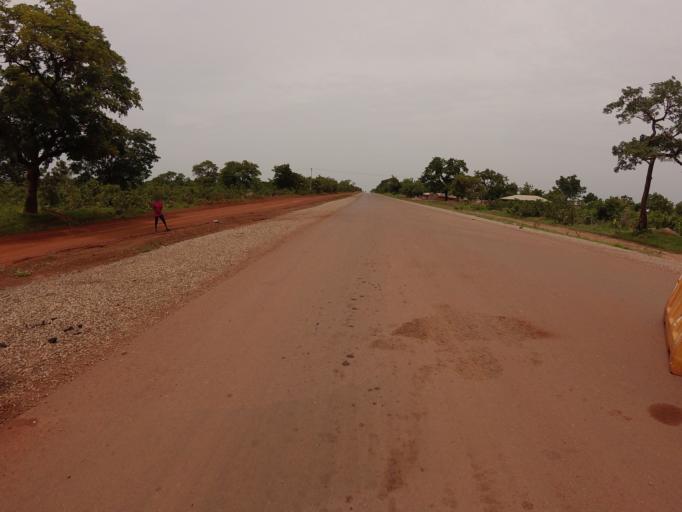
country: GH
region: Northern
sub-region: Yendi
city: Yendi
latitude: 8.9797
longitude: -0.0161
